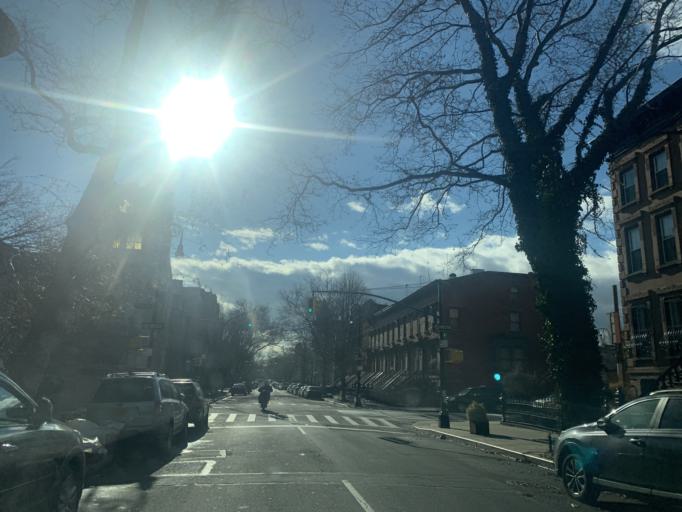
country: US
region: New York
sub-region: Kings County
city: Brooklyn
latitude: 40.6857
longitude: -73.9326
